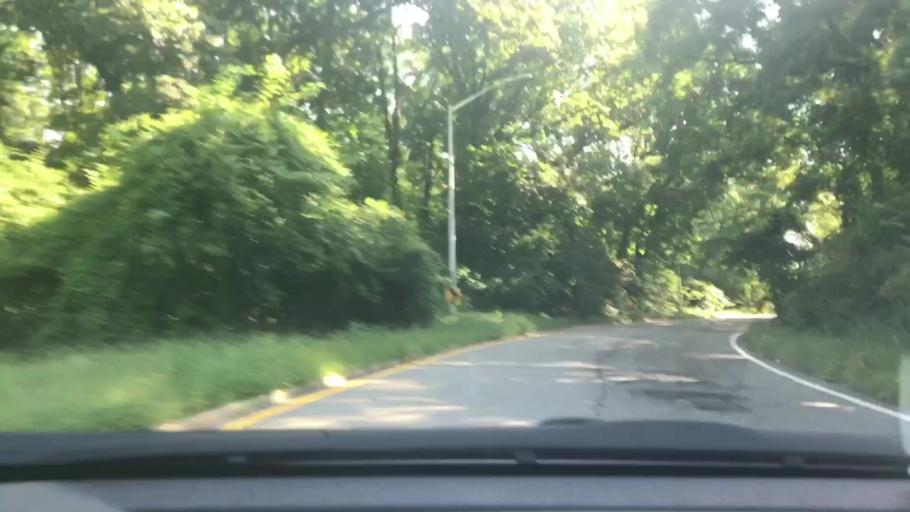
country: US
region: New York
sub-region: Bronx
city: Eastchester
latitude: 40.8708
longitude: -73.8191
